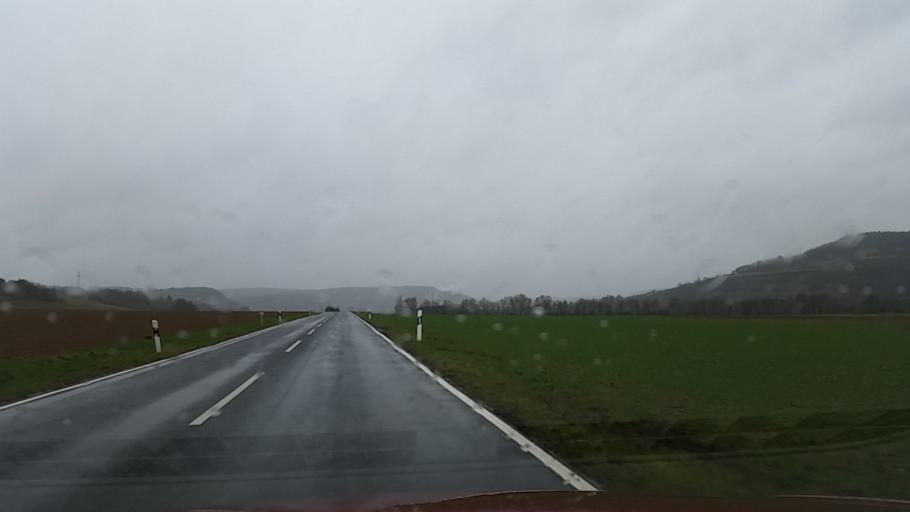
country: DE
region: Bavaria
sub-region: Regierungsbezirk Unterfranken
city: Himmelstadt
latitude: 49.9354
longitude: 9.7920
